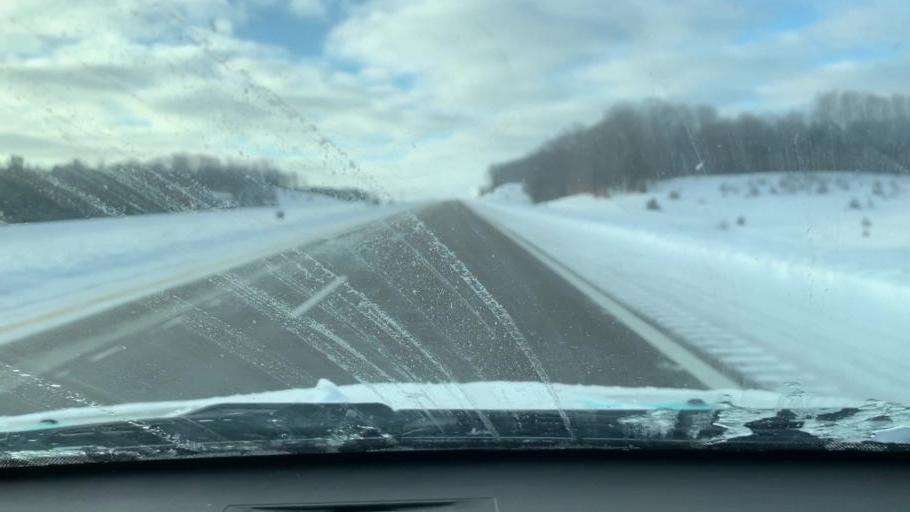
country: US
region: Michigan
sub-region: Wexford County
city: Manton
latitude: 44.3555
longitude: -85.4038
